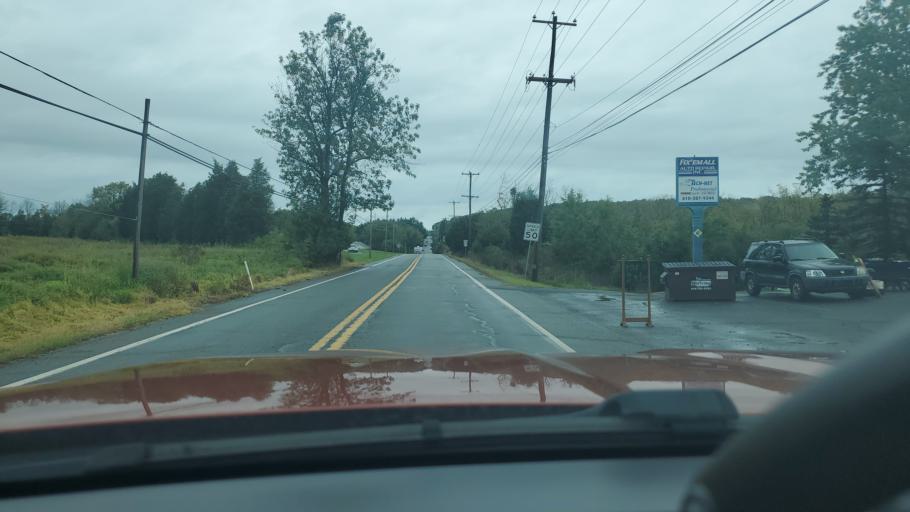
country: US
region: Pennsylvania
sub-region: Montgomery County
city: Spring Mount
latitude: 40.2836
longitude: -75.4812
